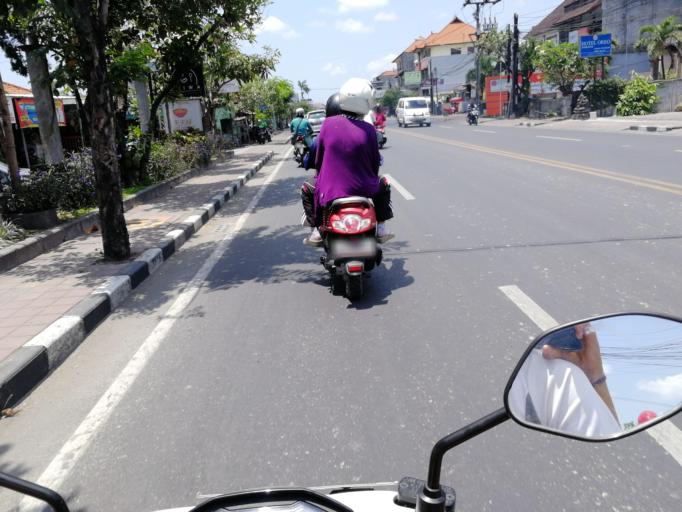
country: ID
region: Bali
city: Banjar Kertasari
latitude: -8.6373
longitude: 115.1967
